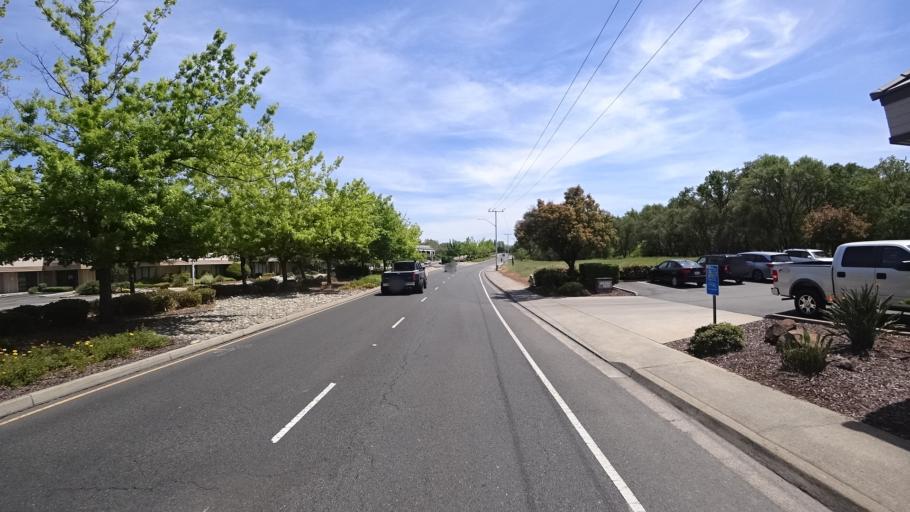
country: US
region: California
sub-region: Placer County
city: Rocklin
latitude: 38.7863
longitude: -121.2517
